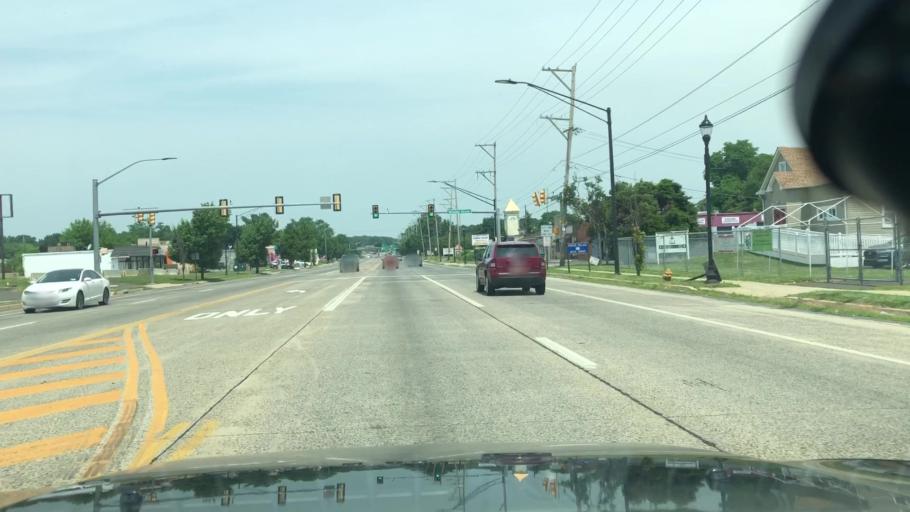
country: US
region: Pennsylvania
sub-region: Bucks County
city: Bristol
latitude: 40.1065
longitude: -74.8767
